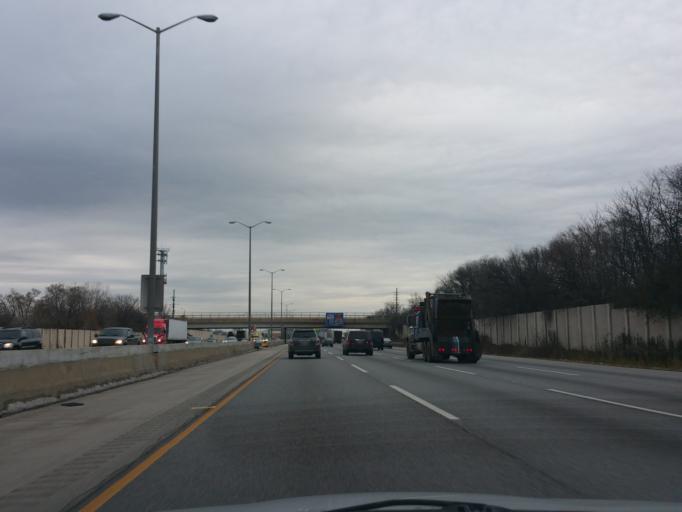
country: US
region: Illinois
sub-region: Cook County
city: Western Springs
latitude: 41.7918
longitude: -87.9081
